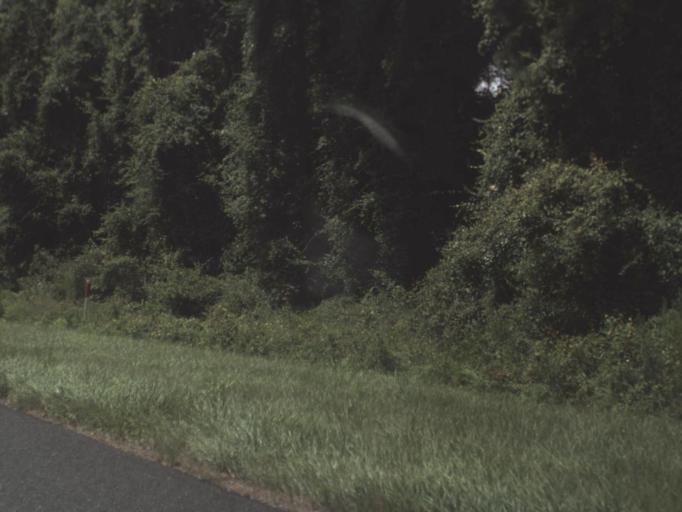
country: US
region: Florida
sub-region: Taylor County
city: Perry
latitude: 30.2045
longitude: -83.6587
